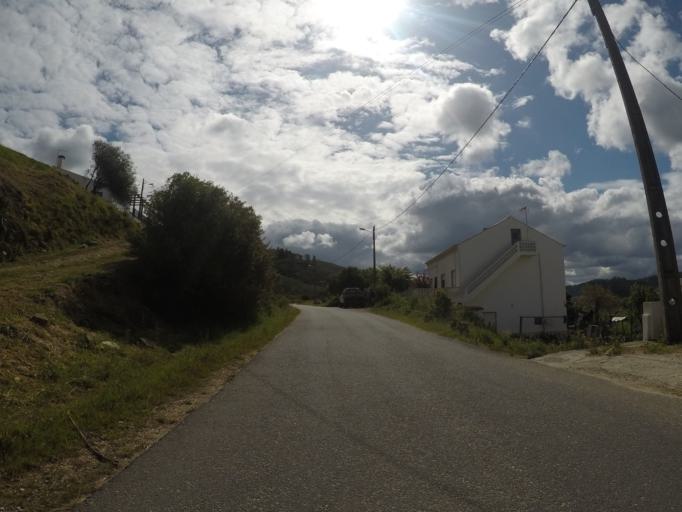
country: PT
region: Beja
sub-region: Odemira
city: Sao Teotonio
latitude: 37.4363
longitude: -8.7671
